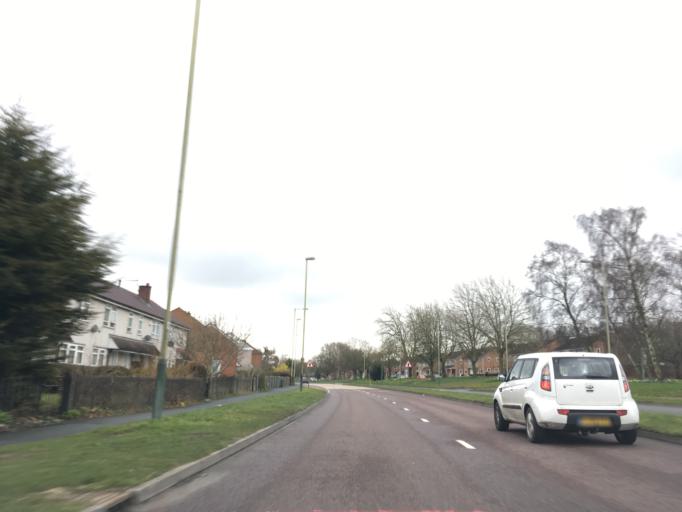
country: GB
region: England
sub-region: Borough of Swindon
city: Swindon
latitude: 51.5483
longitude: -1.7552
